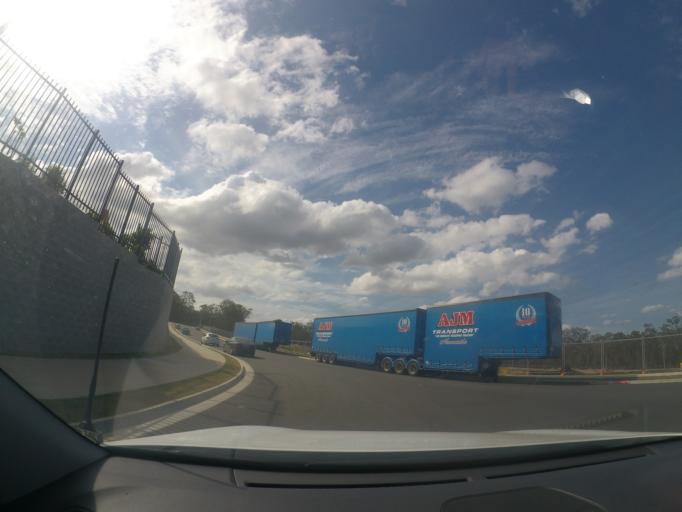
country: AU
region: Queensland
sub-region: Logan
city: Woodridge
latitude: -27.6556
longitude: 153.0841
